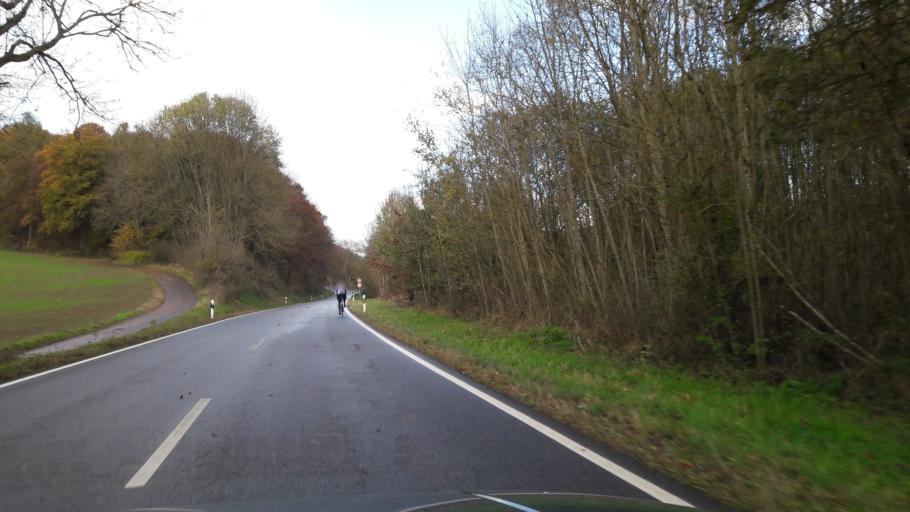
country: DE
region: Rheinland-Pfalz
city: Ohmbach
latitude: 49.4573
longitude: 7.3484
